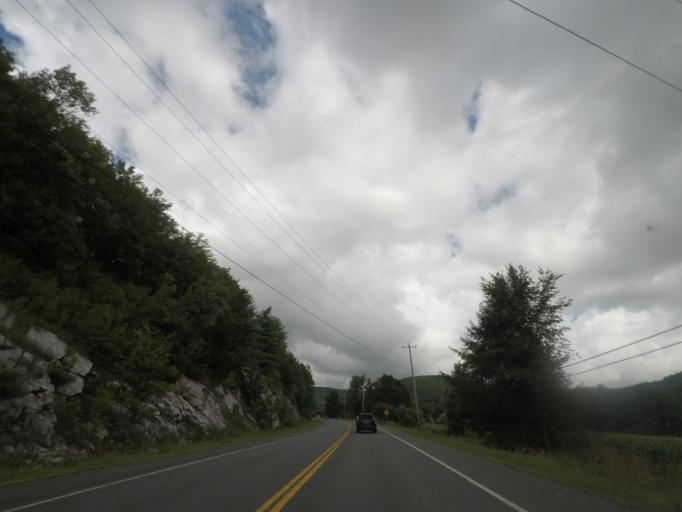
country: US
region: Massachusetts
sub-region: Berkshire County
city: Williamstown
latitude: 42.6787
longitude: -73.3670
